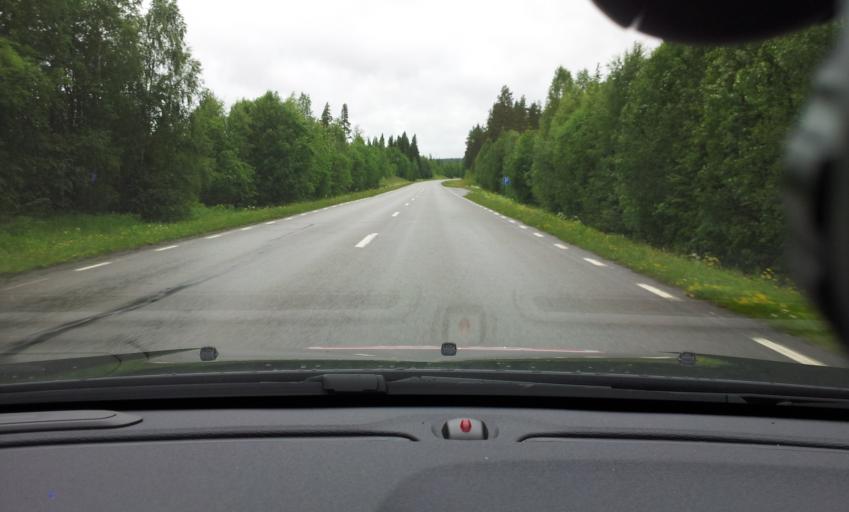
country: SE
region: Jaemtland
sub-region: Krokoms Kommun
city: Krokom
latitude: 63.3970
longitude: 14.4980
